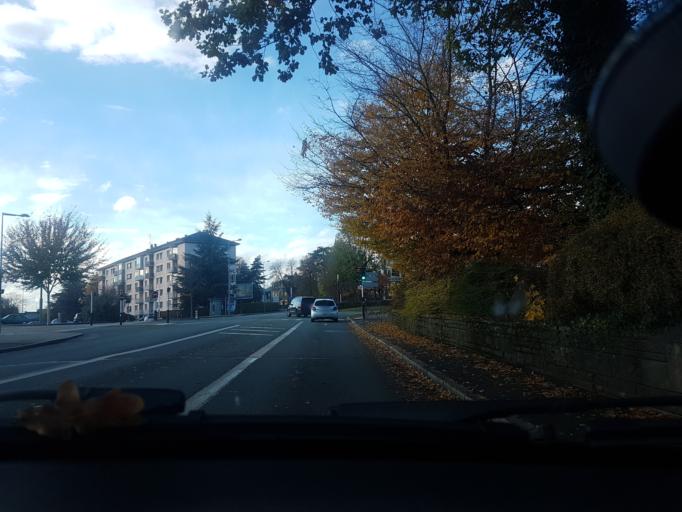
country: FR
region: Franche-Comte
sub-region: Territoire de Belfort
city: Bavilliers
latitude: 47.6363
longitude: 6.8462
